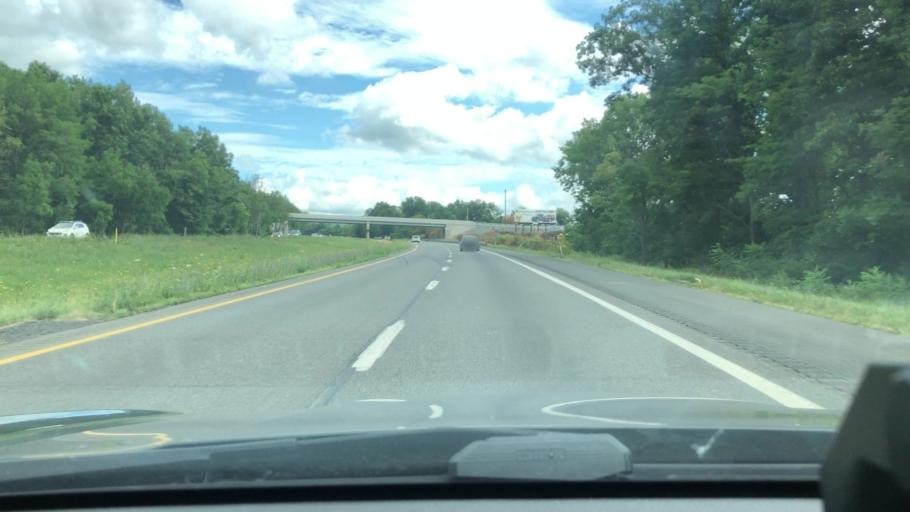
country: US
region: Pennsylvania
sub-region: Northampton County
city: Wind Gap
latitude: 40.8176
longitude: -75.2984
